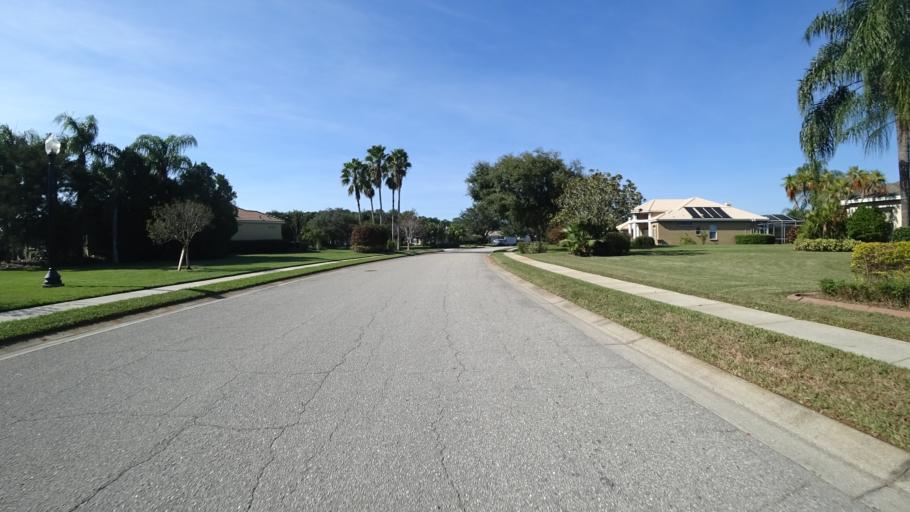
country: US
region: Florida
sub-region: Sarasota County
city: The Meadows
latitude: 27.4085
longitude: -82.4449
